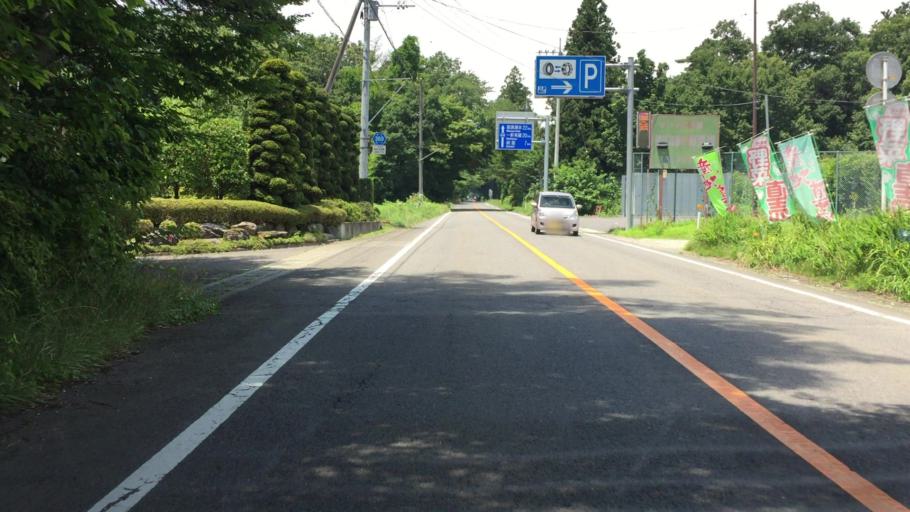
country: JP
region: Tochigi
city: Kuroiso
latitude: 37.0144
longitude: 139.9603
